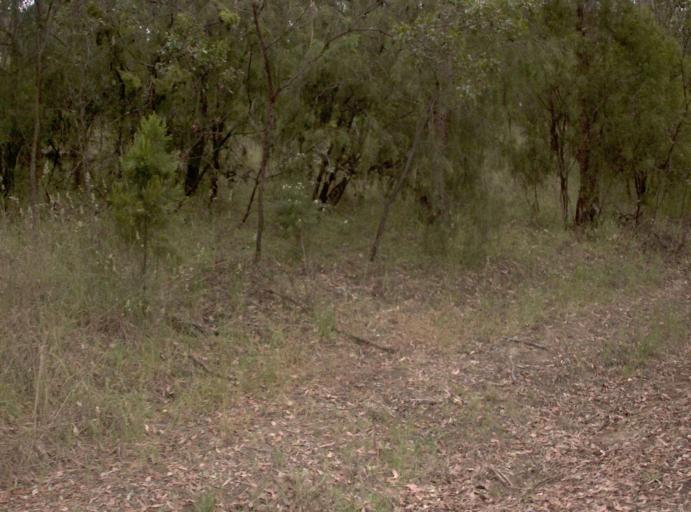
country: AU
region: Victoria
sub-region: East Gippsland
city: Bairnsdale
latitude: -37.7191
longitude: 147.5937
